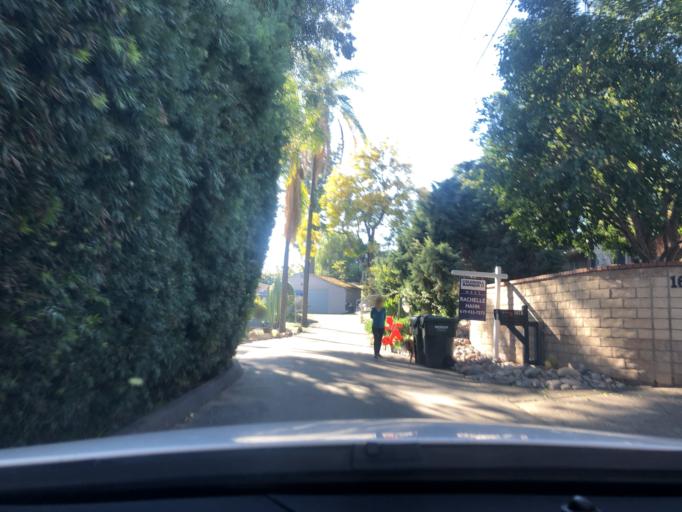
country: US
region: California
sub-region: San Diego County
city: Rancho San Diego
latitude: 32.7674
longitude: -116.9386
